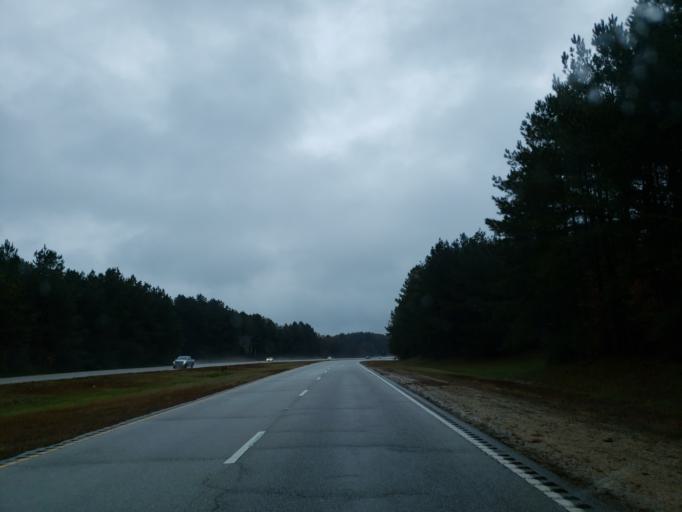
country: US
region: Mississippi
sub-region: Lauderdale County
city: Meridian
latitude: 32.2956
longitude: -88.6952
